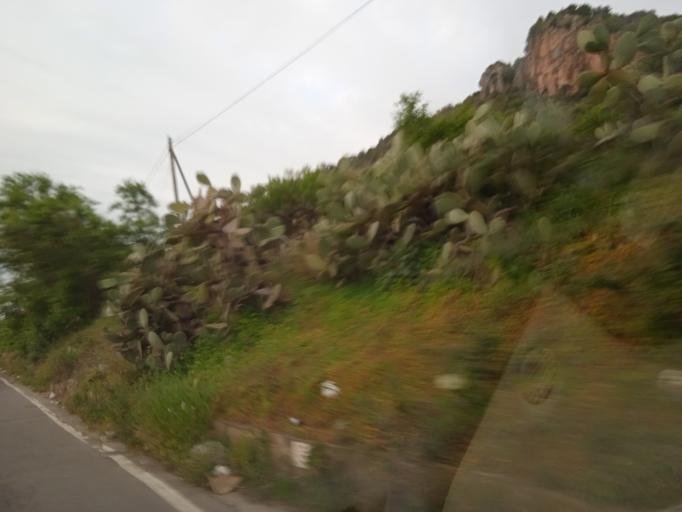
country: IT
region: Sicily
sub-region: Palermo
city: Misilmeri
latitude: 38.0457
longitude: 13.4608
